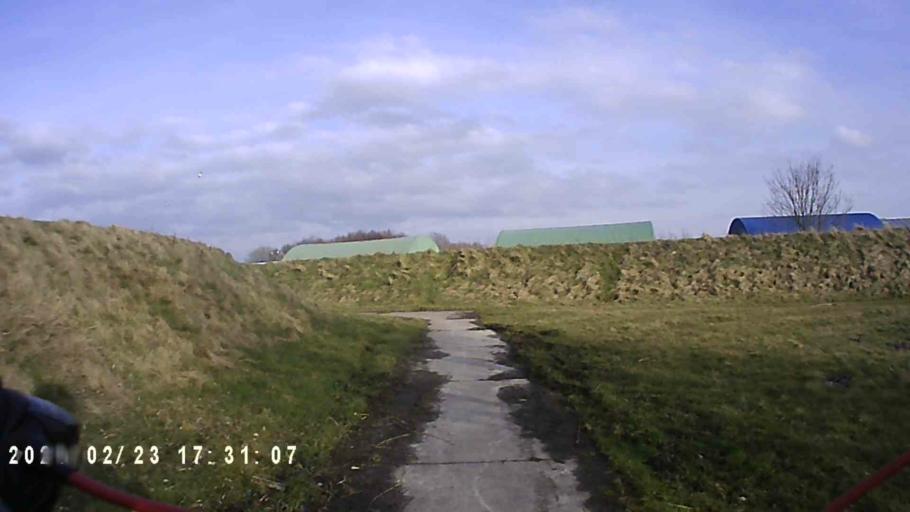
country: NL
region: Groningen
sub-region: Gemeente Winsum
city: Winsum
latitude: 53.3983
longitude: 6.4534
